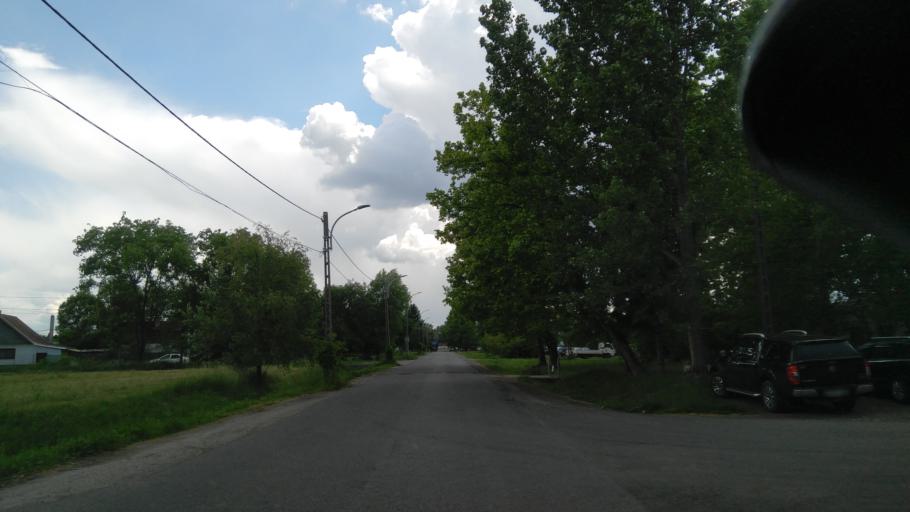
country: HU
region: Bekes
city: Gyula
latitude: 46.6616
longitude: 21.2696
